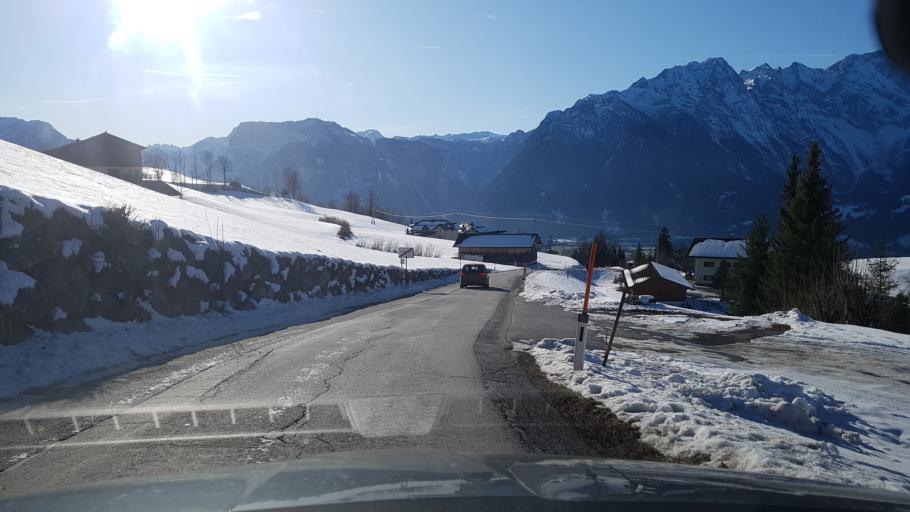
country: AT
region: Salzburg
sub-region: Politischer Bezirk Hallein
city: Golling an der Salzach
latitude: 47.6321
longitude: 13.1983
